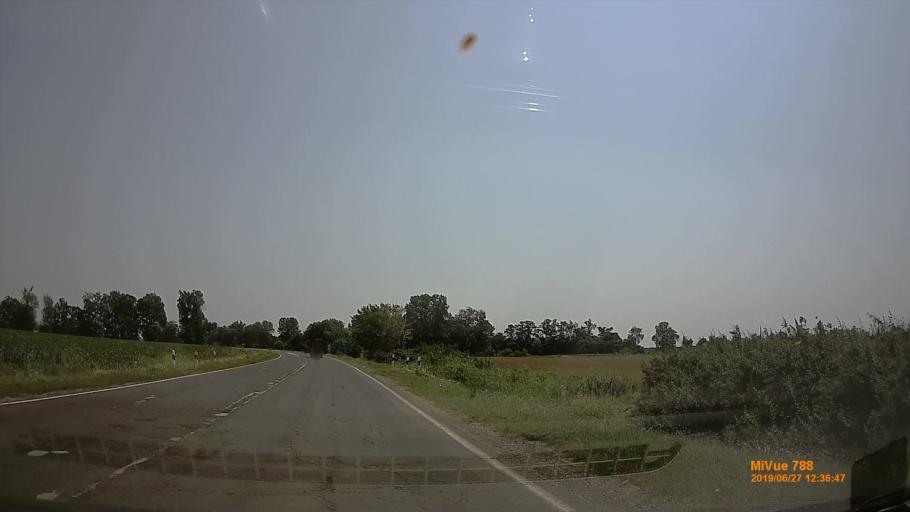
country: HU
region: Pest
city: Tortel
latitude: 47.1870
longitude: 19.9266
